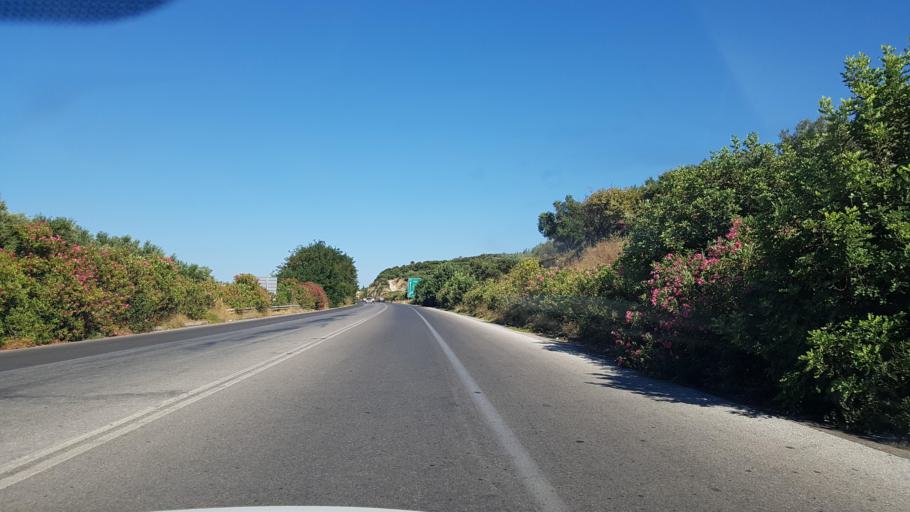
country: GR
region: Crete
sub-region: Nomos Chanias
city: Kolympari
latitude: 35.5247
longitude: 23.8036
